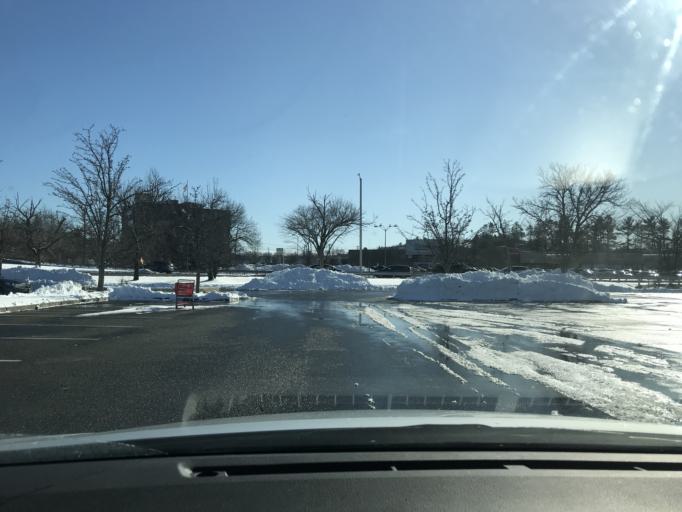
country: US
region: Massachusetts
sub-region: Essex County
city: Saugus
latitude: 42.4810
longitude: -71.0241
